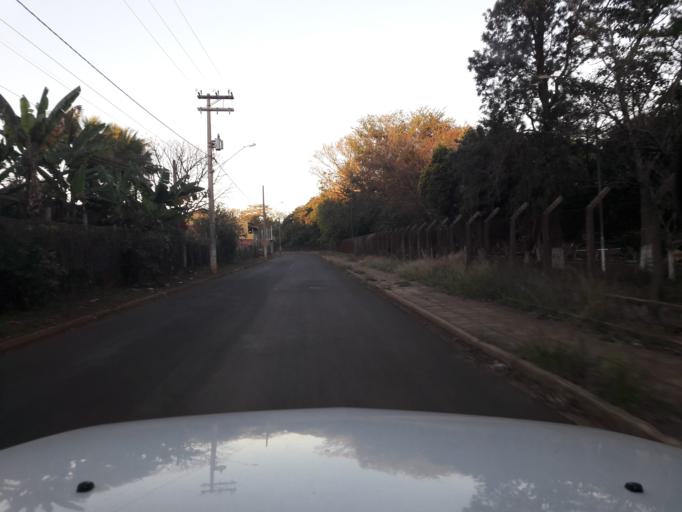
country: BR
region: Sao Paulo
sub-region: Moji-Guacu
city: Mogi-Gaucu
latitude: -22.3413
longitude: -46.9332
